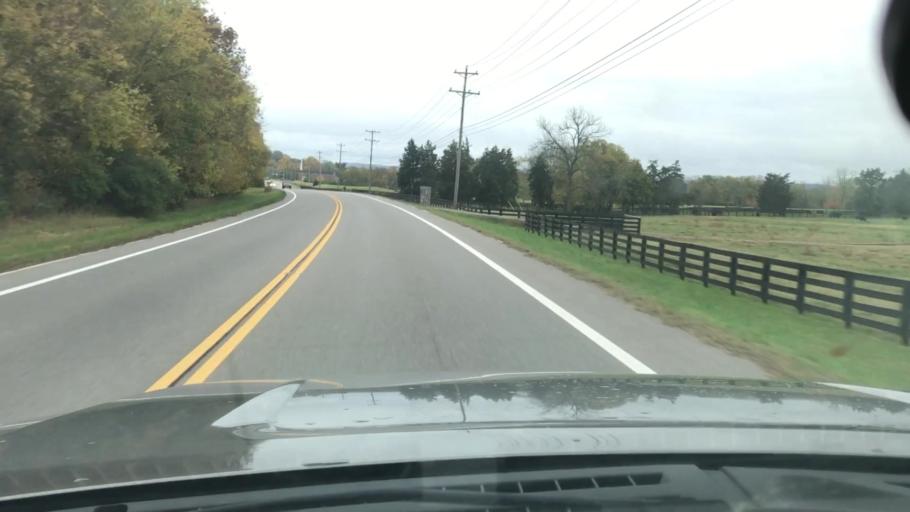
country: US
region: Tennessee
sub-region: Williamson County
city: Franklin
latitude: 35.9866
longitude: -86.8907
